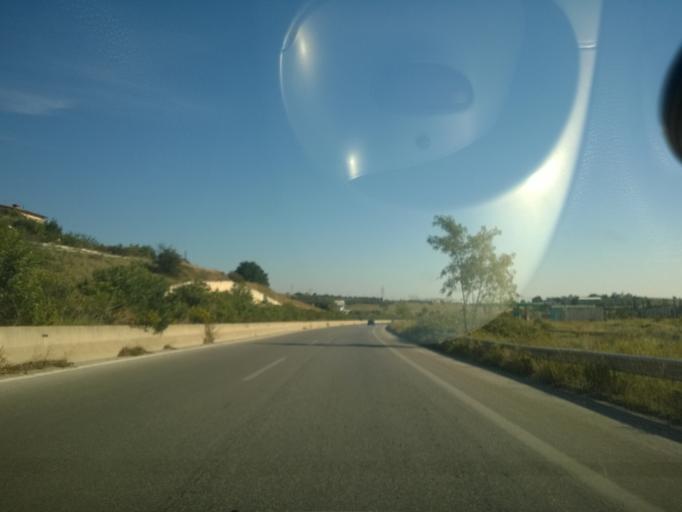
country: GR
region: Central Macedonia
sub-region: Nomos Thessalonikis
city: Kardia
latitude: 40.4519
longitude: 23.0085
